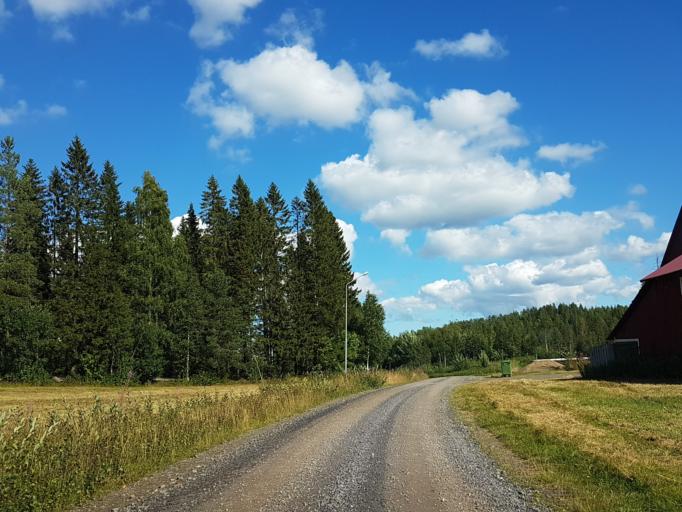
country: SE
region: Vaesterbotten
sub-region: Skelleftea Kommun
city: Burtraesk
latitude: 64.2930
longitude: 20.4634
